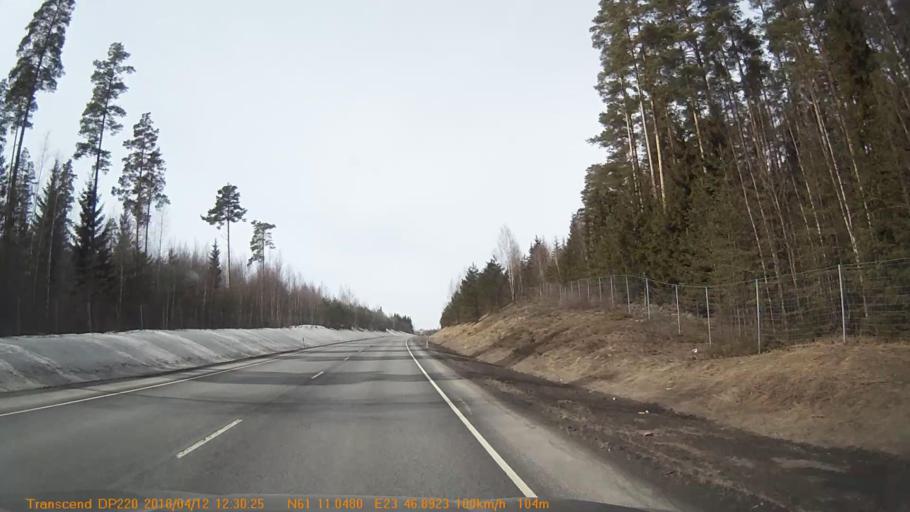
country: FI
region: Pirkanmaa
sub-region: Etelae-Pirkanmaa
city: Viiala
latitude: 61.1842
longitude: 23.7807
